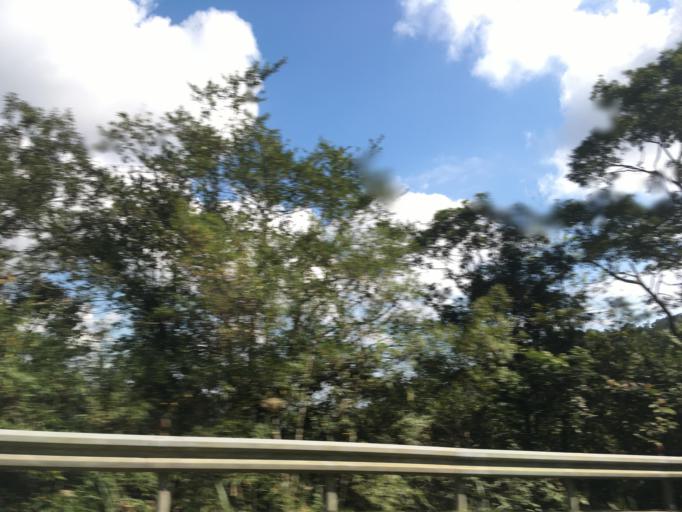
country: TW
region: Taiwan
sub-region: Yilan
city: Yilan
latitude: 24.7491
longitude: 121.6463
